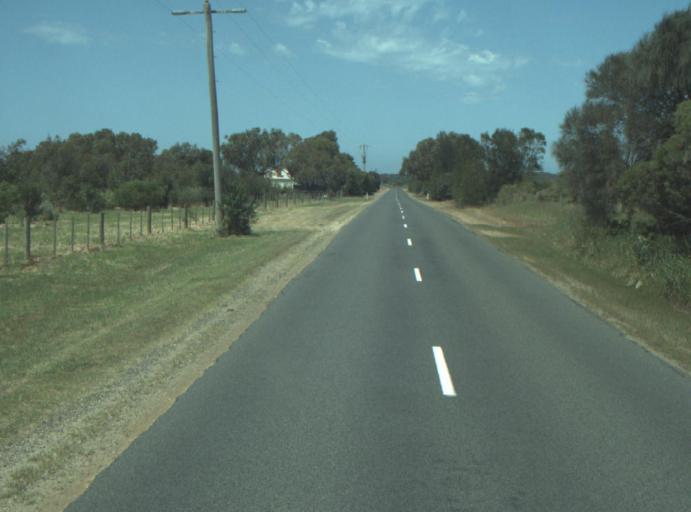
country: AU
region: Victoria
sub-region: Greater Geelong
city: Breakwater
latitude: -38.2805
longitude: 144.4015
